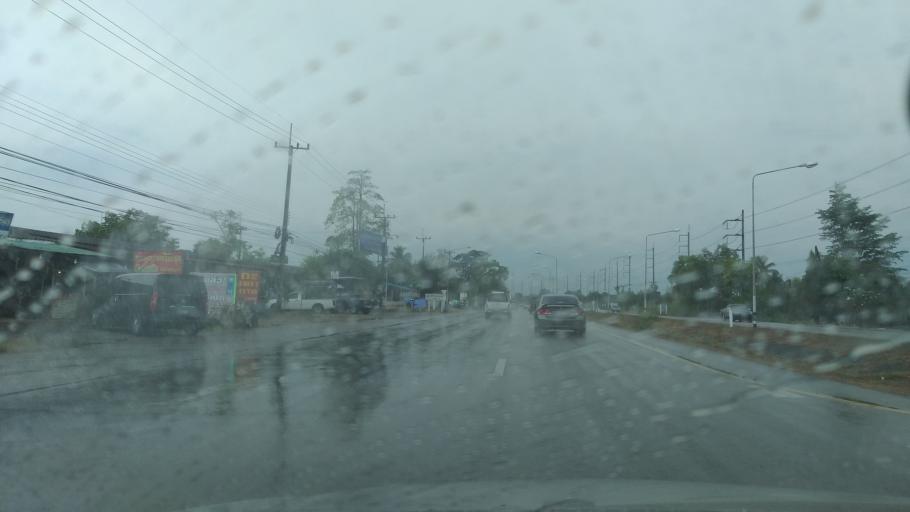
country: TH
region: Trat
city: Khao Saming
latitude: 12.3952
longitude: 102.3577
